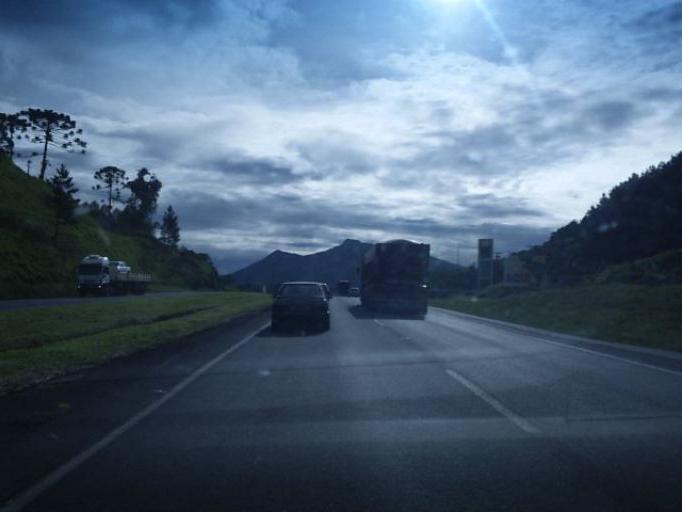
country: BR
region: Parana
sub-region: Antonina
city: Antonina
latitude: -25.1081
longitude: -48.7438
